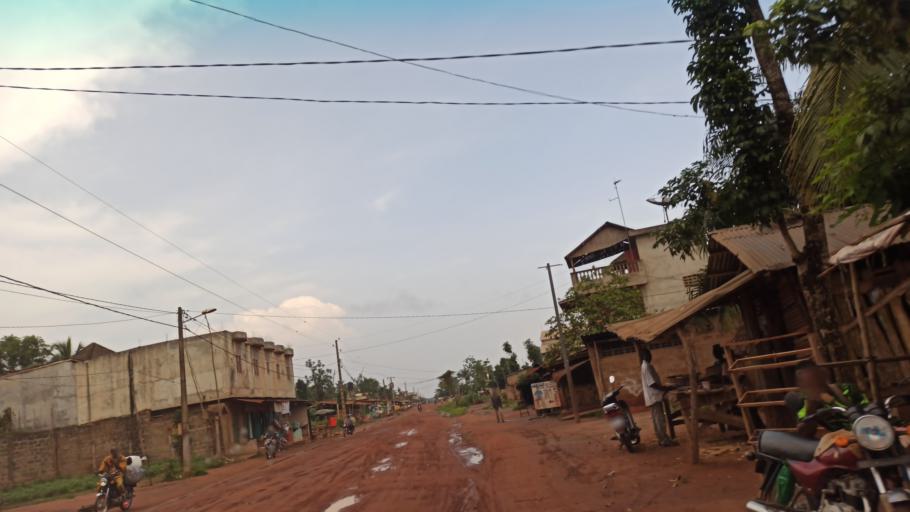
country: BJ
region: Queme
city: Porto-Novo
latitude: 6.4899
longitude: 2.6660
